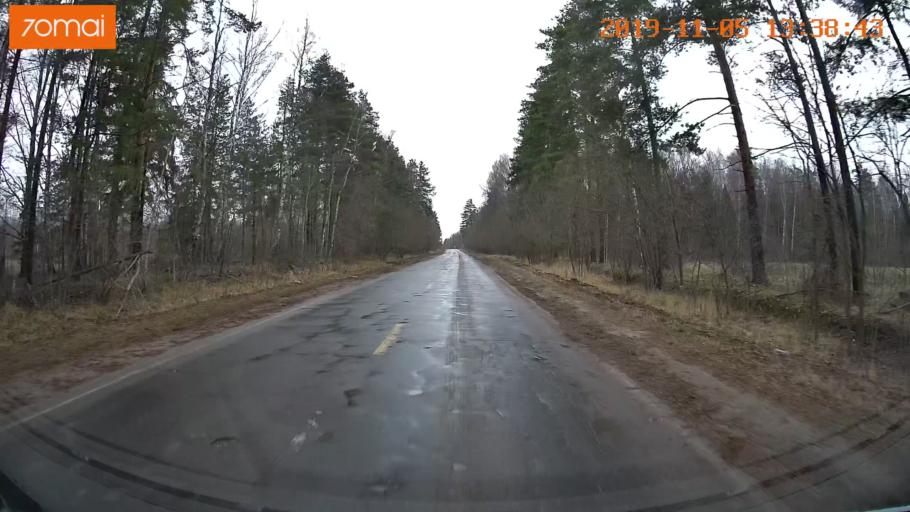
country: RU
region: Ivanovo
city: Shuya
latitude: 56.9341
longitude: 41.3869
